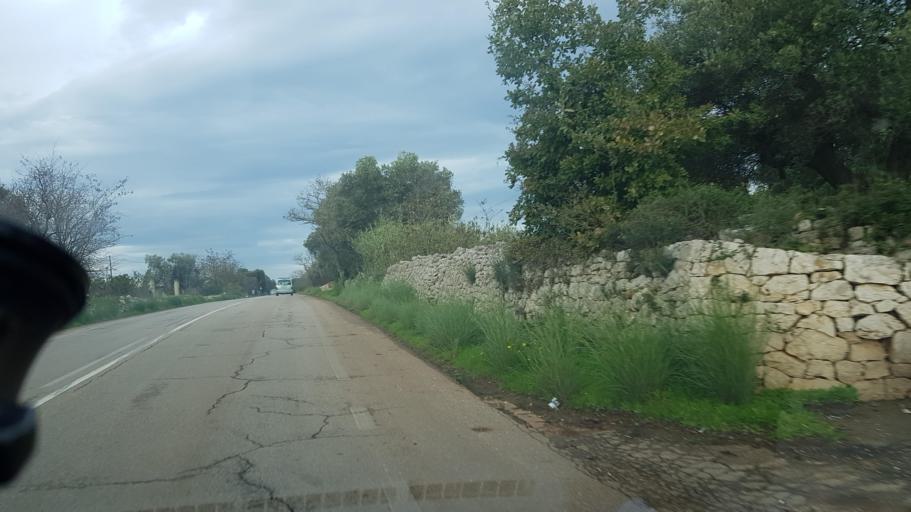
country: IT
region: Apulia
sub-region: Provincia di Brindisi
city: Carovigno
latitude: 40.6862
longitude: 17.6782
